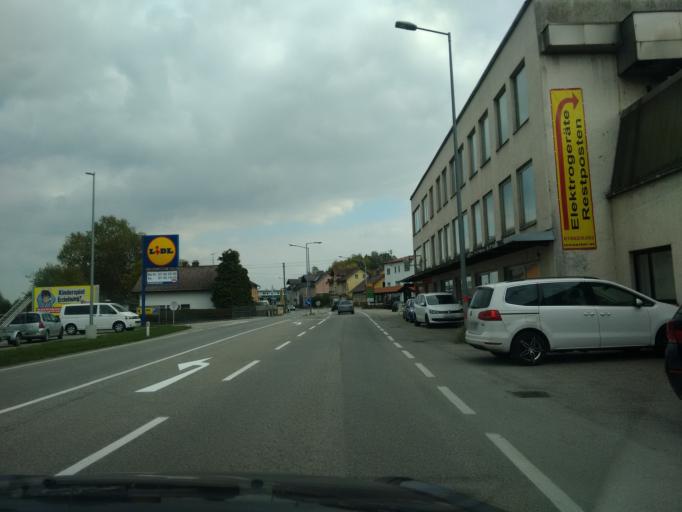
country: AT
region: Upper Austria
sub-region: Politischer Bezirk Vocklabruck
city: Attnang-Puchheim
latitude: 48.0056
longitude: 13.7063
